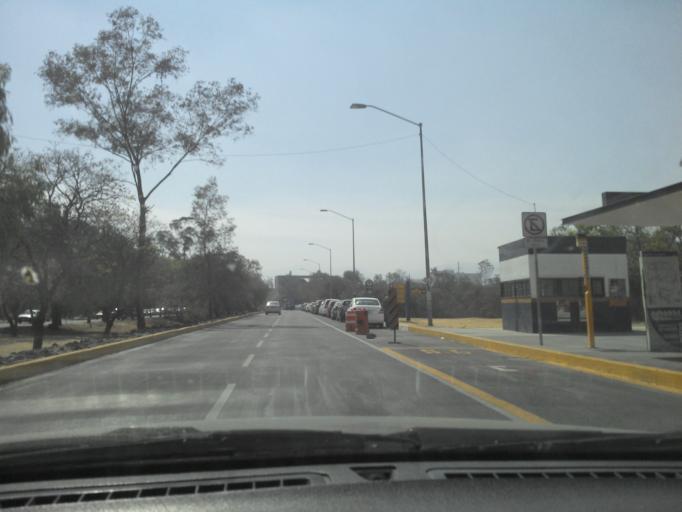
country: MX
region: Mexico City
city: Tlalpan
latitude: 19.3146
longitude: -99.1863
